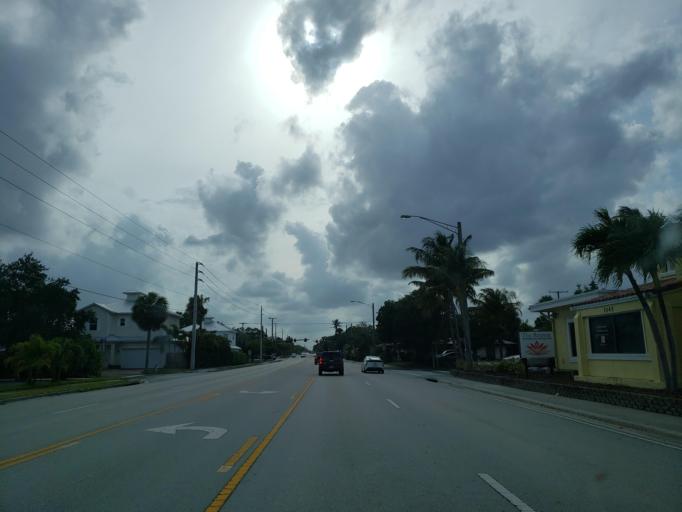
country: US
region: Florida
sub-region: Martin County
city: Stuart
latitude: 27.1975
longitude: -80.2343
